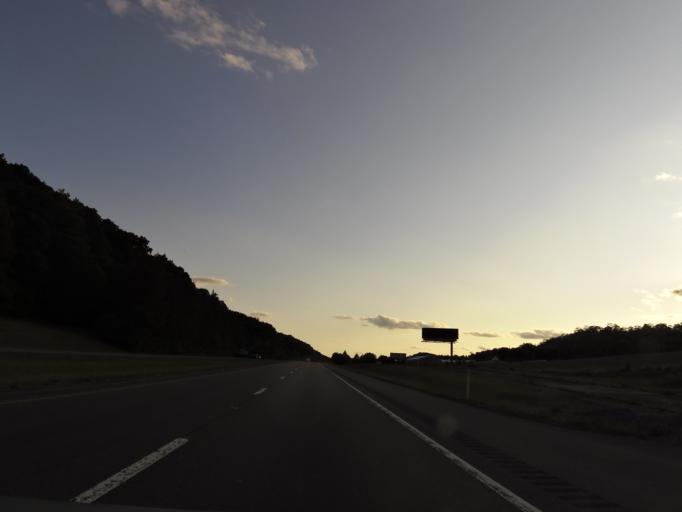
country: US
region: Tennessee
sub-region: Sullivan County
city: Walnut Hill
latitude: 36.5829
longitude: -82.2685
